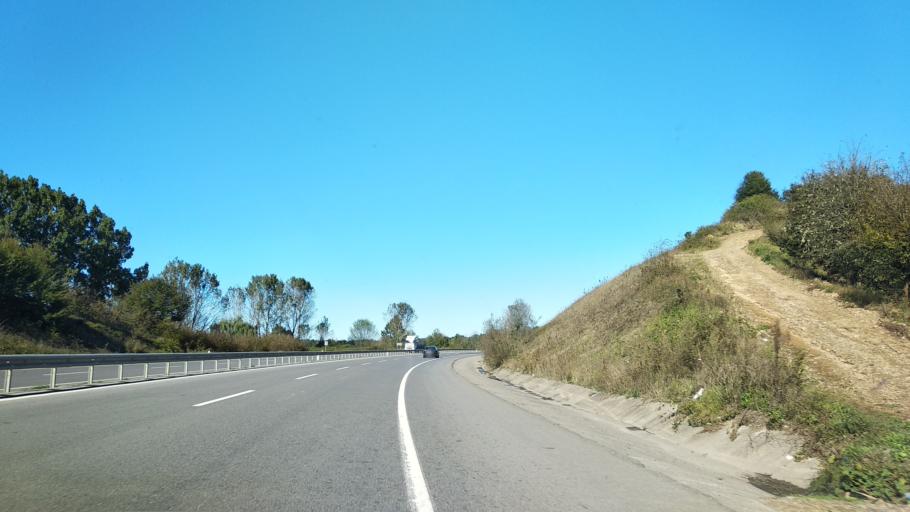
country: TR
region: Sakarya
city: Karasu
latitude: 41.0603
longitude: 30.6373
